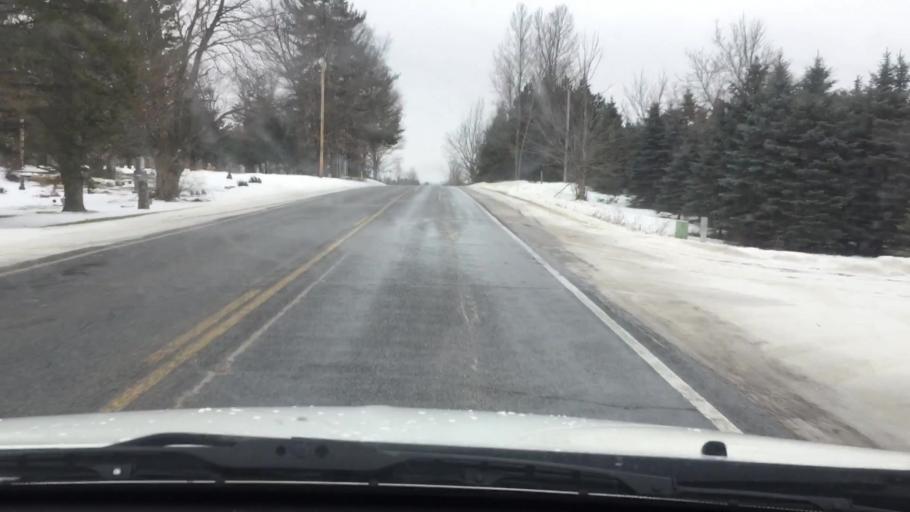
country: US
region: Michigan
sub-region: Wexford County
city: Cadillac
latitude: 44.0676
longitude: -85.4440
